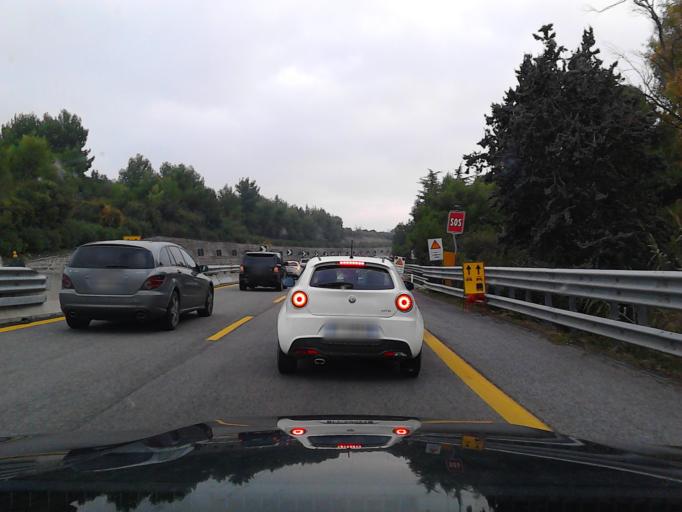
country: IT
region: Abruzzo
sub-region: Provincia di Teramo
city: Tortoreto Lido
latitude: 42.7882
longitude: 13.9348
